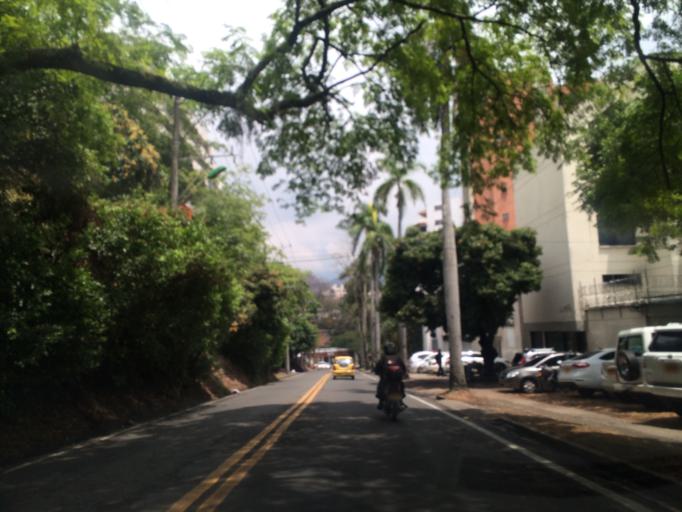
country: CO
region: Valle del Cauca
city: Cali
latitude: 3.4497
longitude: -76.5457
